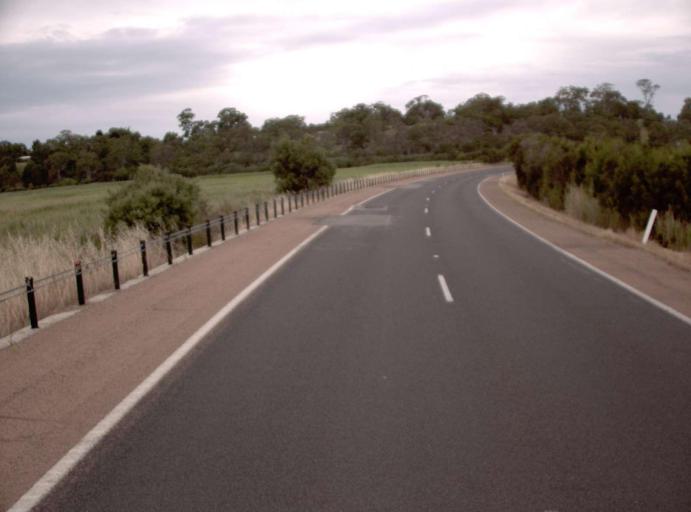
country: AU
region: Victoria
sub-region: East Gippsland
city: Bairnsdale
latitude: -37.8855
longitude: 147.6596
